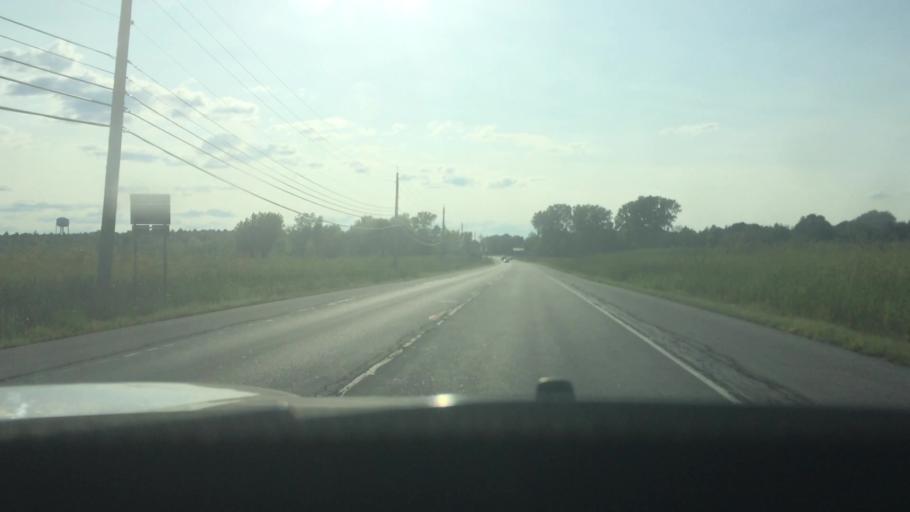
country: US
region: New York
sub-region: St. Lawrence County
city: Potsdam
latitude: 44.6674
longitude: -75.0134
